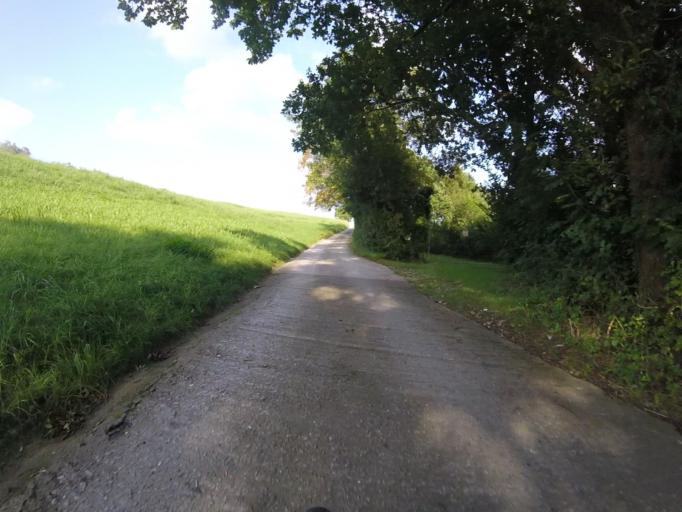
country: ES
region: Basque Country
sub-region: Provincia de Guipuzcoa
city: Fuenterrabia
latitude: 43.3517
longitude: -1.8194
